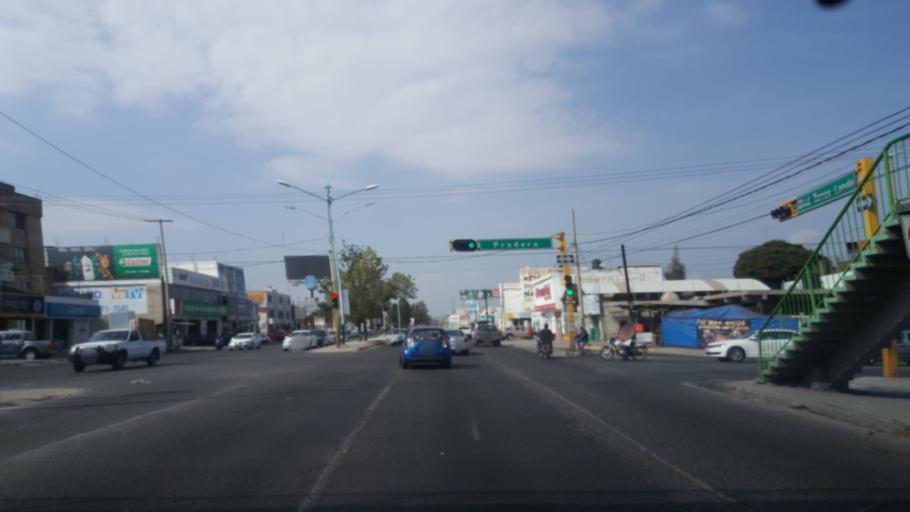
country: MX
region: Guanajuato
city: Leon
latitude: 21.0968
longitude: -101.6501
